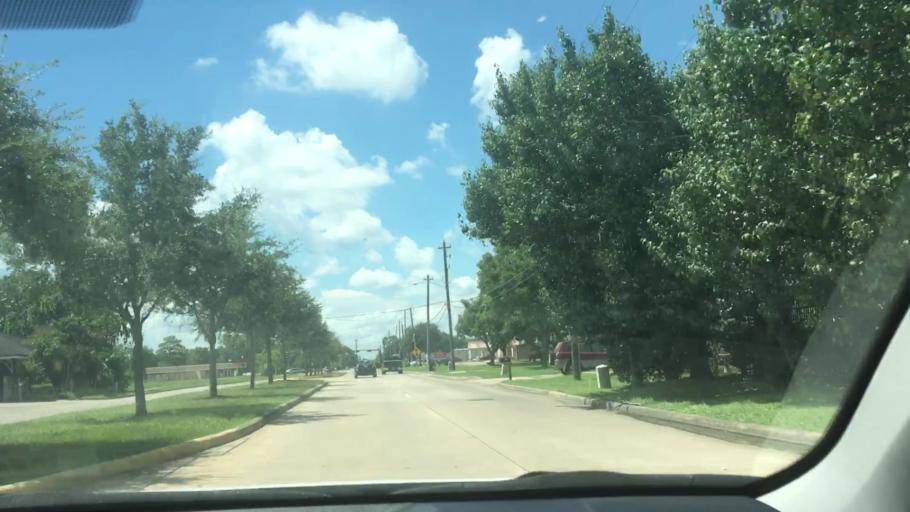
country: US
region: Texas
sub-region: Fort Bend County
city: Fifth Street
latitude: 29.6065
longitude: -95.5468
